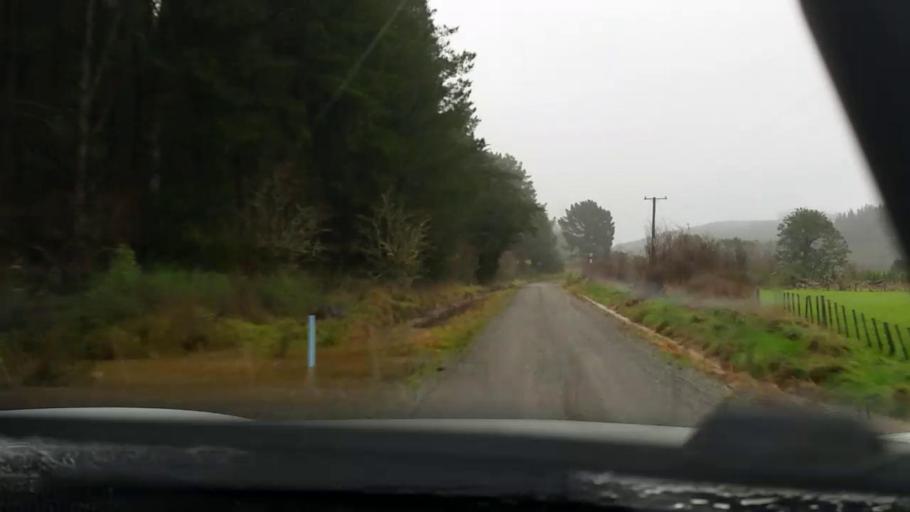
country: NZ
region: Wellington
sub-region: Masterton District
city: Masterton
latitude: -41.1811
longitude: 175.8276
